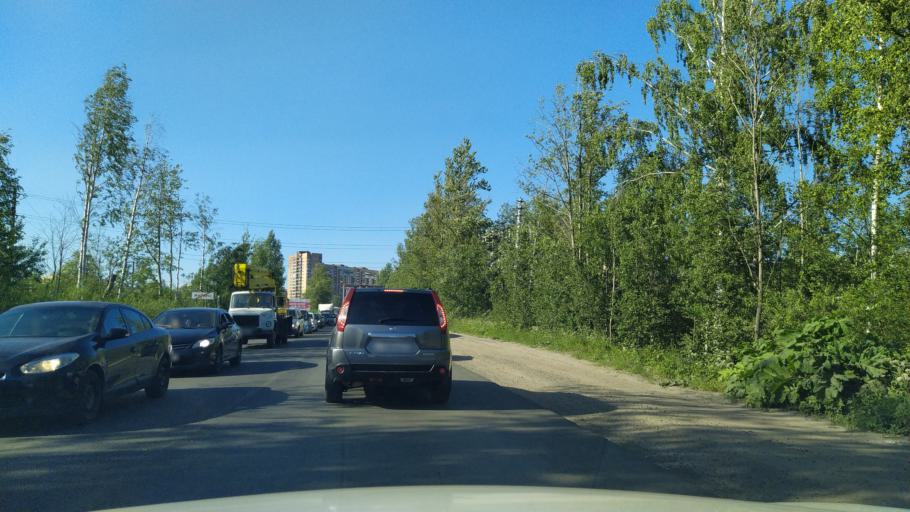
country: RU
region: Leningrad
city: Murino
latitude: 60.0499
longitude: 30.4656
